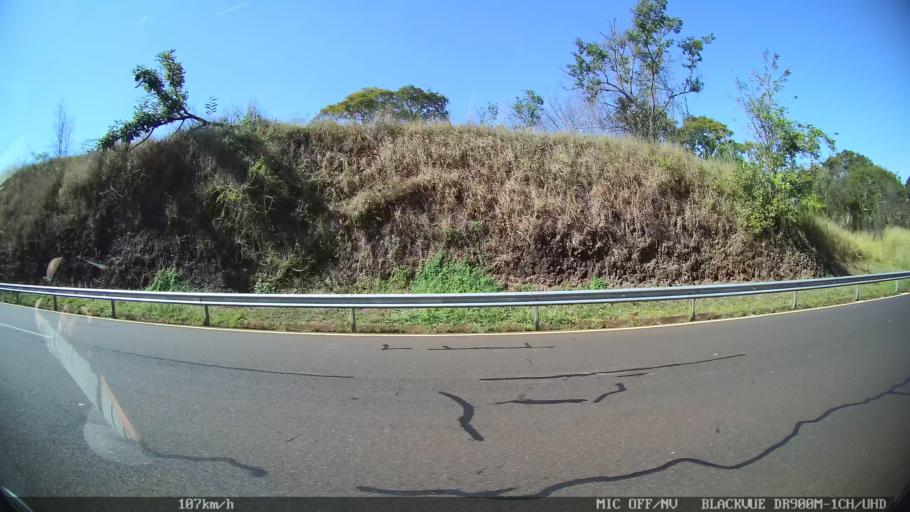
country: BR
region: Sao Paulo
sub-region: Franca
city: Franca
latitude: -20.6158
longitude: -47.4569
